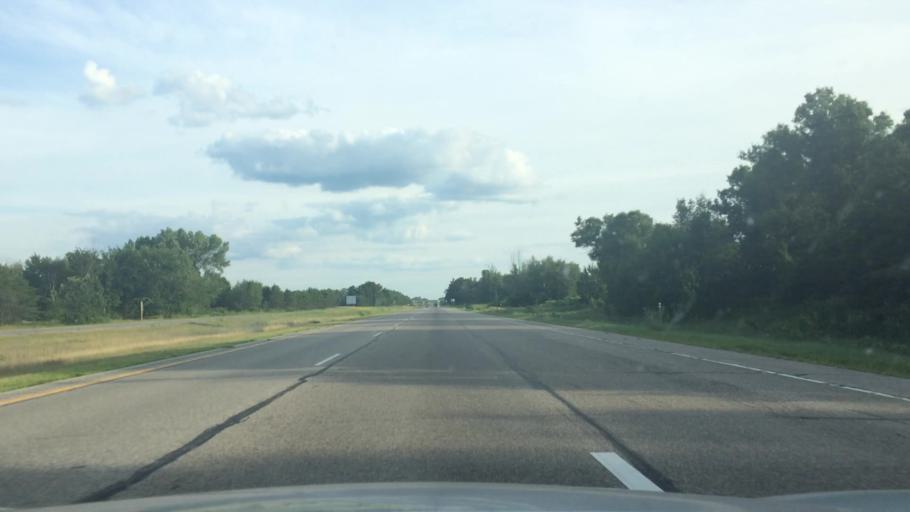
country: US
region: Wisconsin
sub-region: Portage County
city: Plover
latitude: 44.3048
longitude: -89.5237
